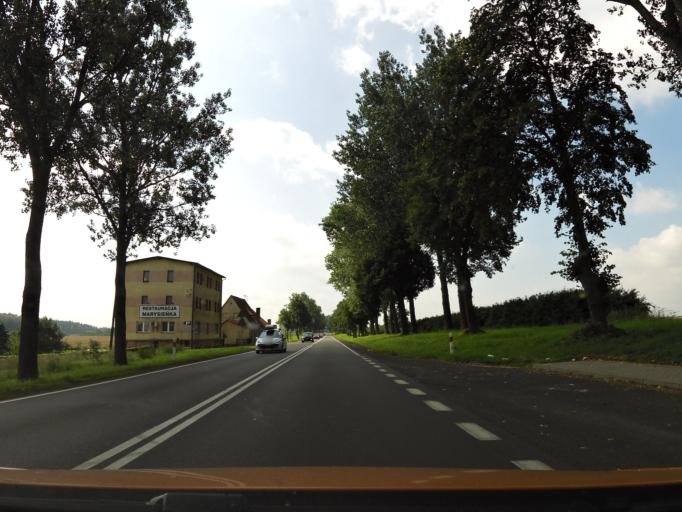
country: PL
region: West Pomeranian Voivodeship
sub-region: Powiat gryficki
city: Ploty
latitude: 53.7716
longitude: 15.2434
